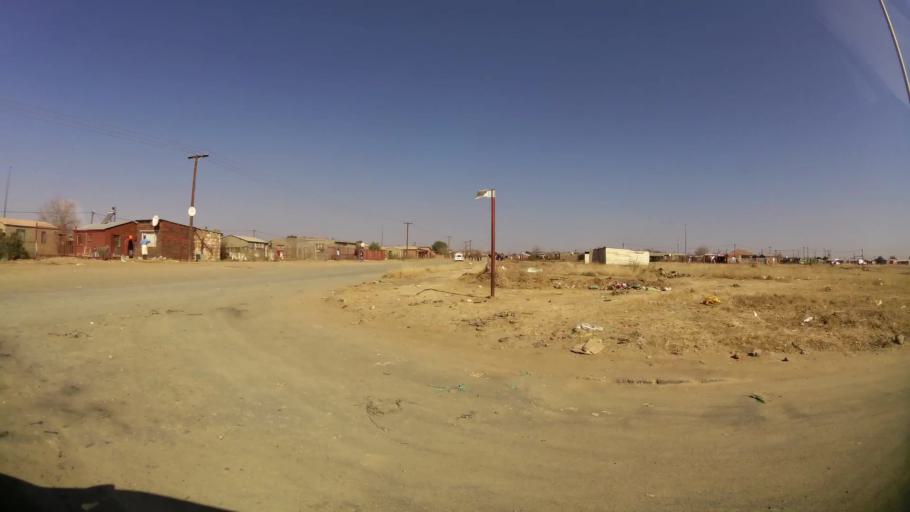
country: ZA
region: Orange Free State
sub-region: Mangaung Metropolitan Municipality
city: Bloemfontein
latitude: -29.1974
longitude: 26.2619
